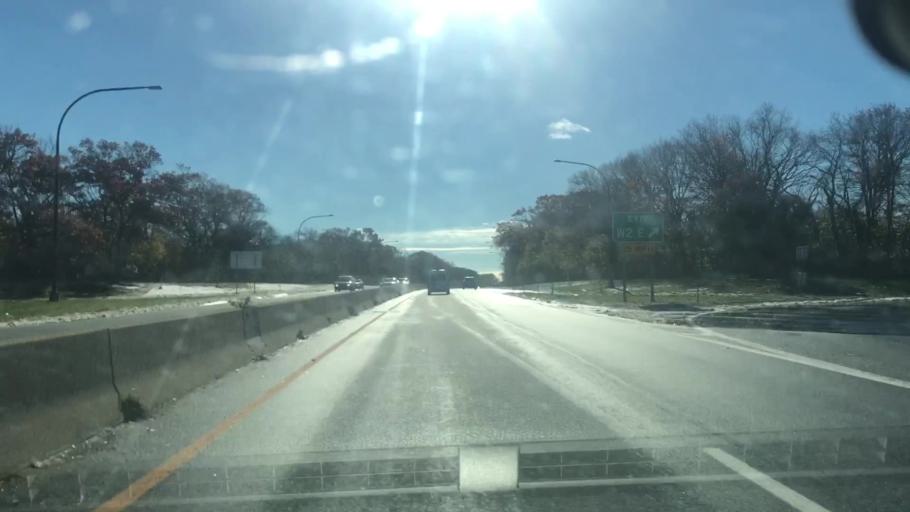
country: US
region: New York
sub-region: Nassau County
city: Salisbury
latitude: 40.7558
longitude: -73.5502
